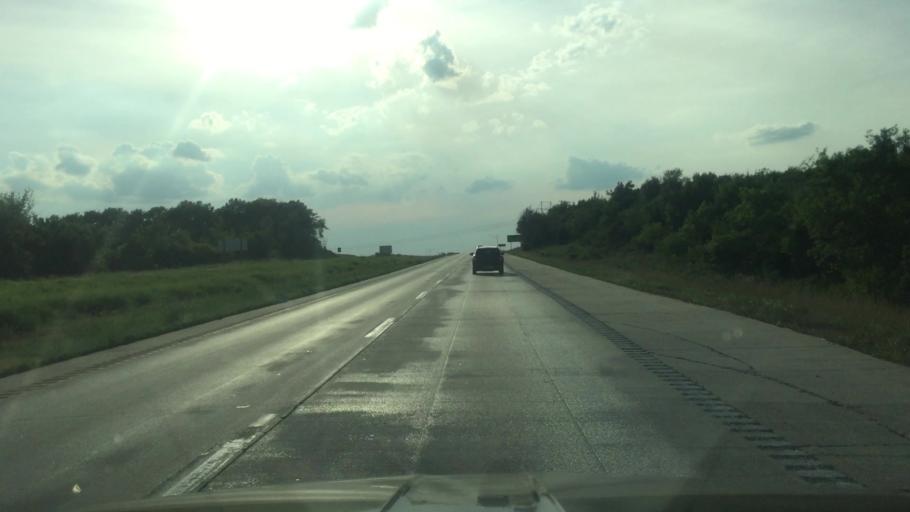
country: US
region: Missouri
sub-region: Jackson County
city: Lone Jack
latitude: 38.8702
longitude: -94.1844
